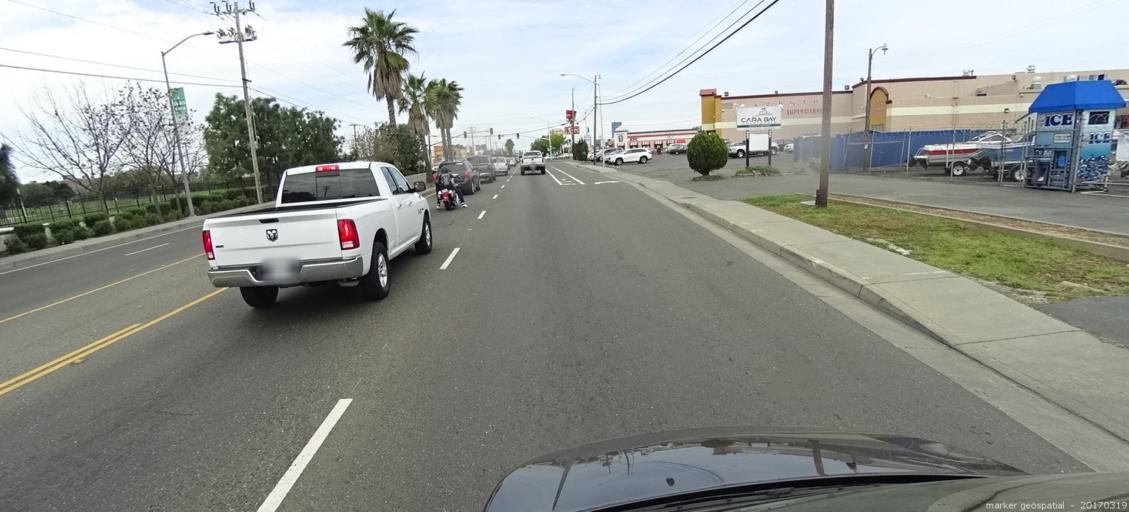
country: US
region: California
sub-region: Sacramento County
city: Parkway
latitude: 38.5147
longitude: -121.4378
